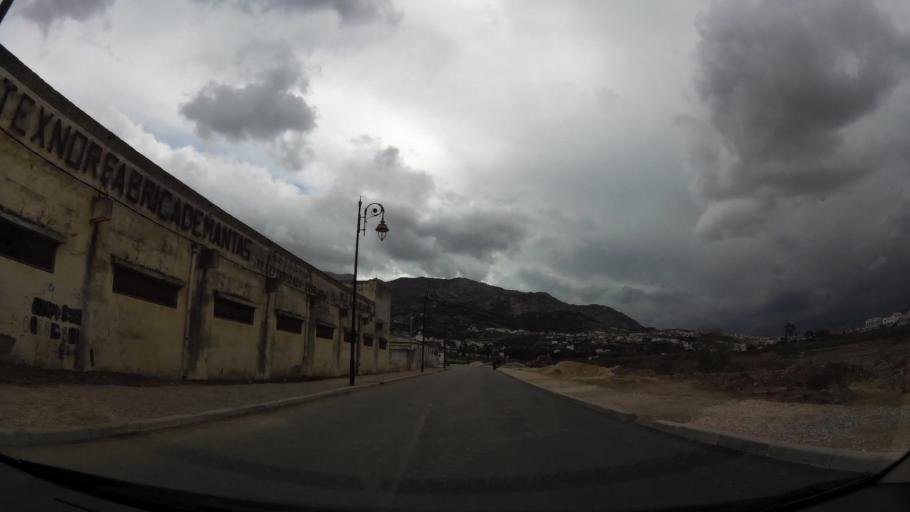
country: MA
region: Tanger-Tetouan
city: Tetouan
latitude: 35.5582
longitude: -5.3513
